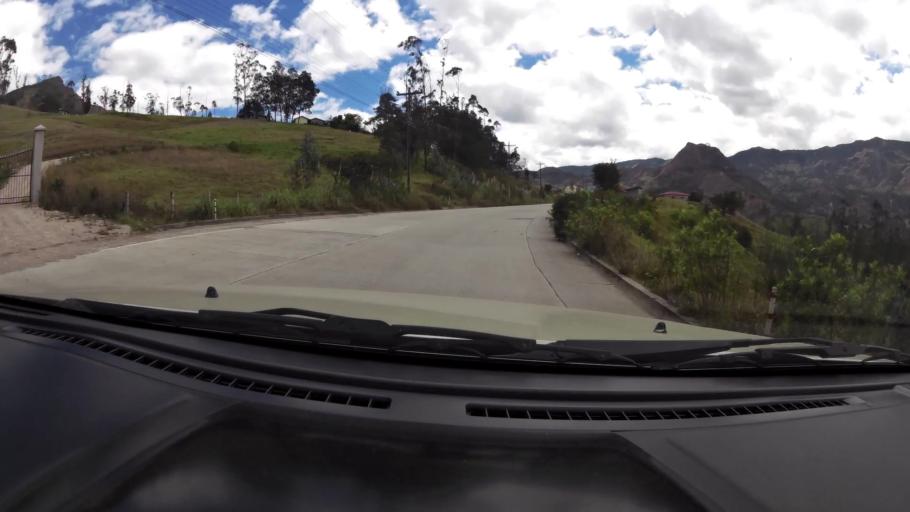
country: EC
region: Azuay
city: Cuenca
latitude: -3.1444
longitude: -79.1429
